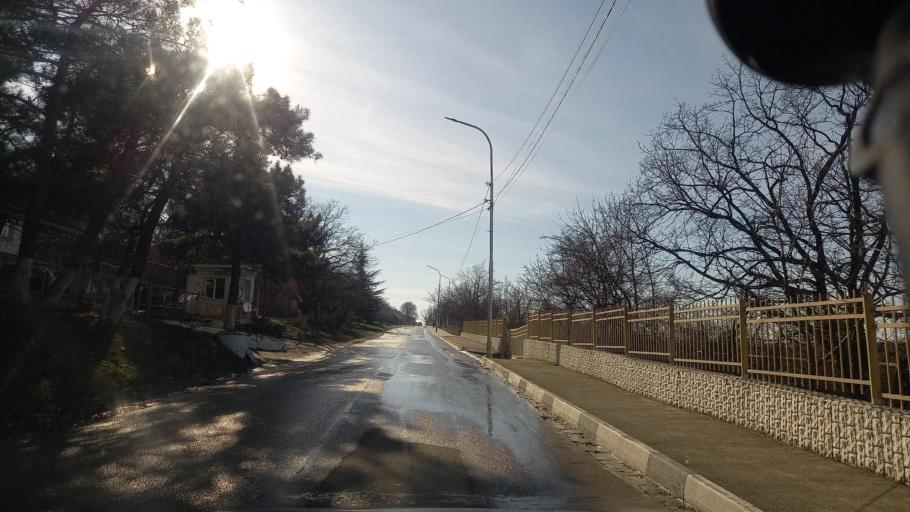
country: RU
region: Krasnodarskiy
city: Kabardinka
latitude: 44.6379
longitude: 37.9200
